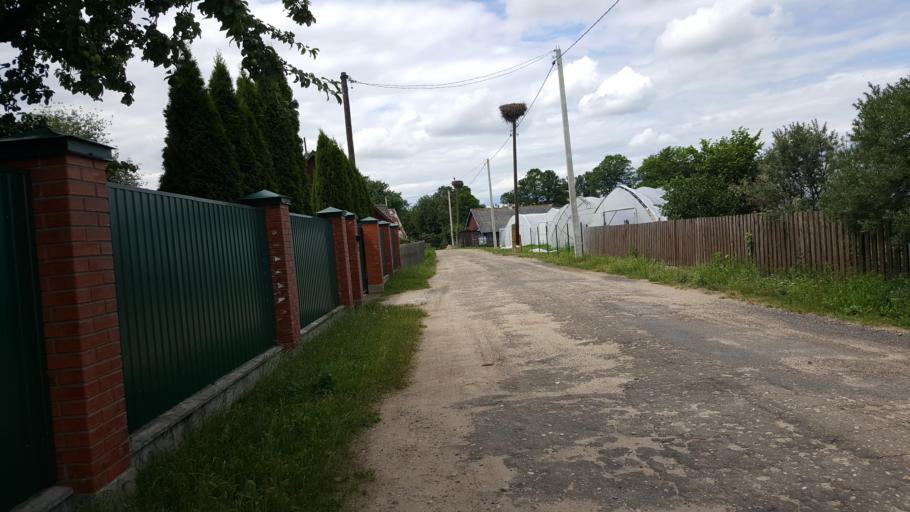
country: BY
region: Brest
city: Kamyanyets
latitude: 52.3708
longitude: 23.8987
